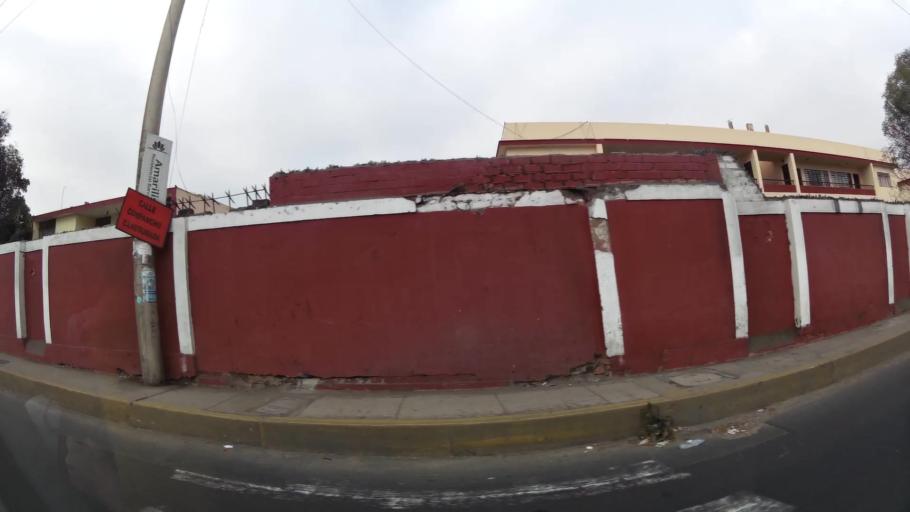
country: PE
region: Lima
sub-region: Lima
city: Surco
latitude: -12.1545
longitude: -77.0194
